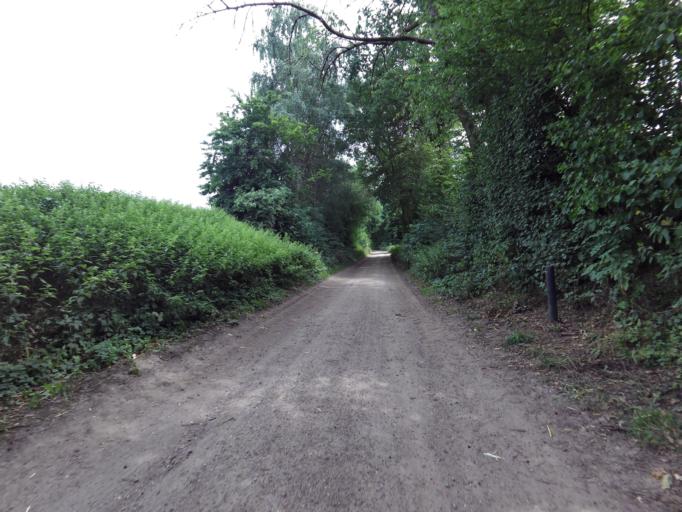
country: NL
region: Limburg
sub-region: Gemeente Simpelveld
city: Simpelveld
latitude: 50.8105
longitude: 5.9858
